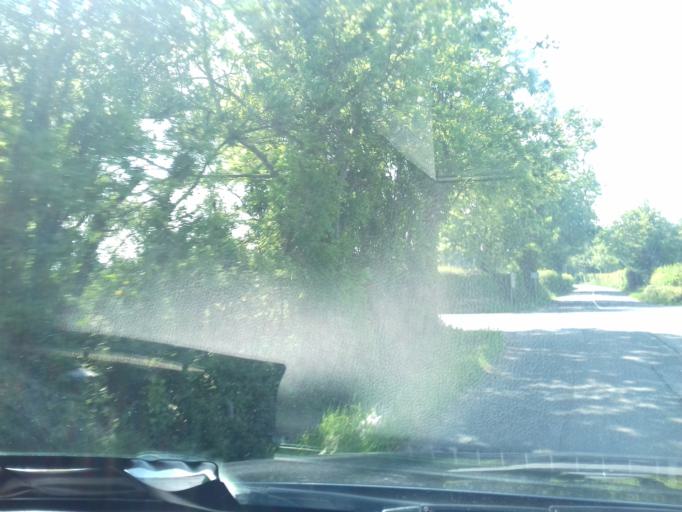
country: IE
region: Leinster
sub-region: Fingal County
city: Swords
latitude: 53.5140
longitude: -6.2350
